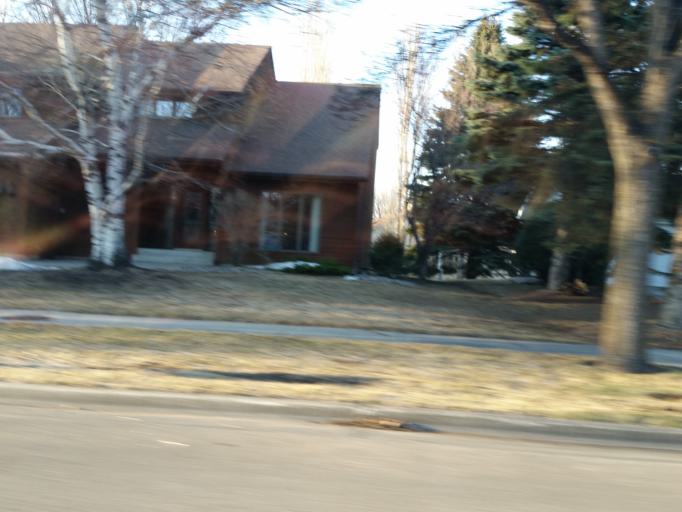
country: US
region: North Dakota
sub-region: Grand Forks County
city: Grand Forks
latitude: 47.8774
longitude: -97.0275
